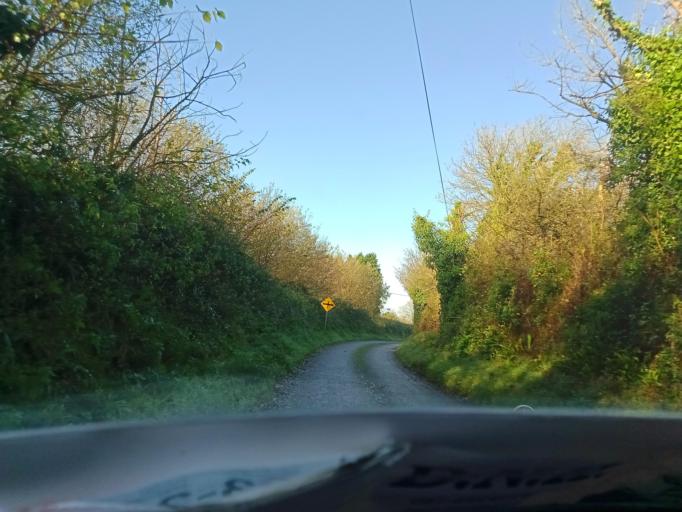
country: IE
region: Leinster
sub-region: Kilkenny
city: Mooncoin
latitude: 52.2932
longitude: -7.1804
